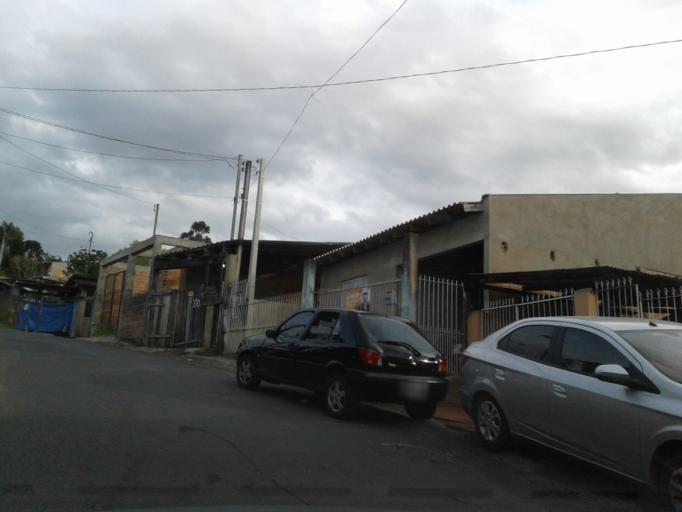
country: BR
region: Rio Grande do Sul
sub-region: Porto Alegre
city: Porto Alegre
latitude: -30.0605
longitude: -51.1461
